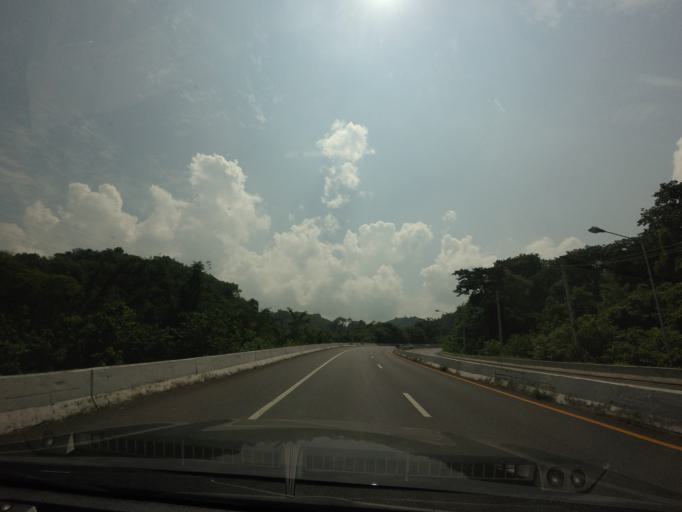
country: TH
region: Phrae
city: Den Chai
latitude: 17.8746
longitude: 100.0458
